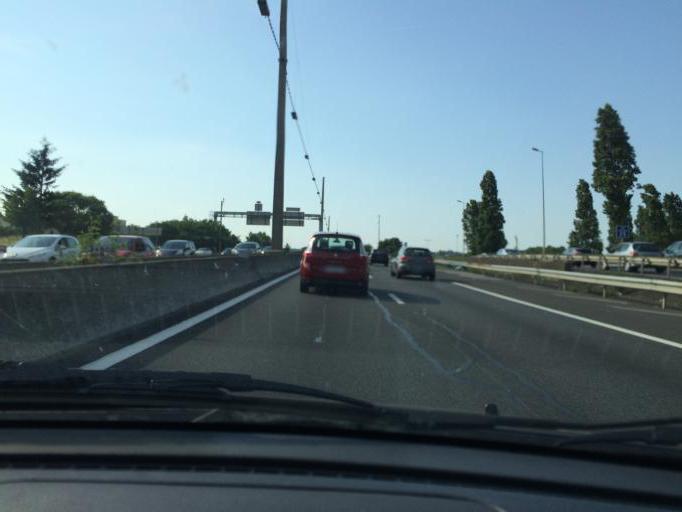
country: FR
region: Rhone-Alpes
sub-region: Departement du Rhone
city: Villeurbanne
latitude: 45.7818
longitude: 4.8931
